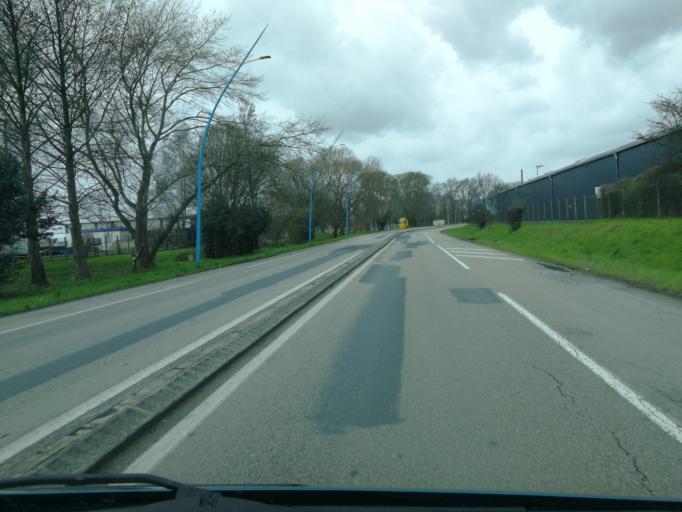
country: FR
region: Haute-Normandie
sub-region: Departement de l'Eure
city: Quillebeuf-sur-Seine
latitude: 49.4757
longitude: 0.5338
